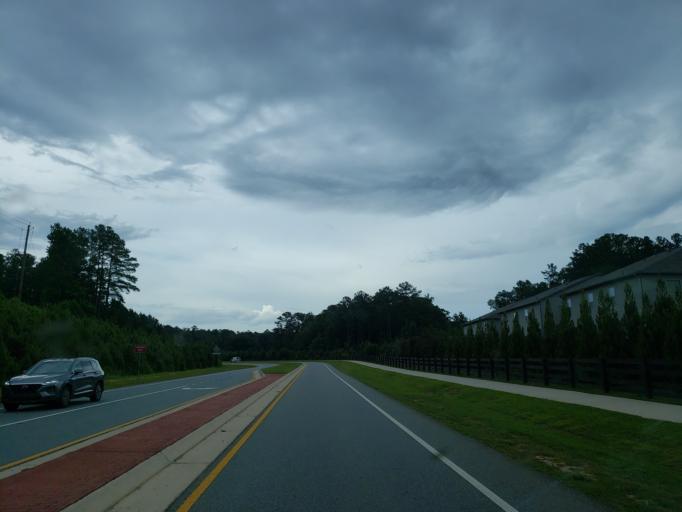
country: US
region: Georgia
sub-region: Cobb County
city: Acworth
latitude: 34.0288
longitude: -84.7517
